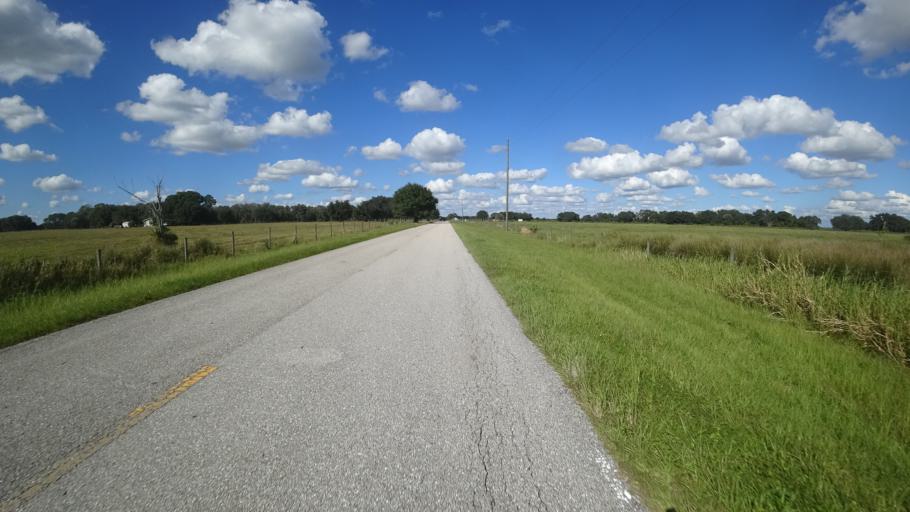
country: US
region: Florida
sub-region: Sarasota County
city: North Port
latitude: 27.1988
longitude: -82.1223
